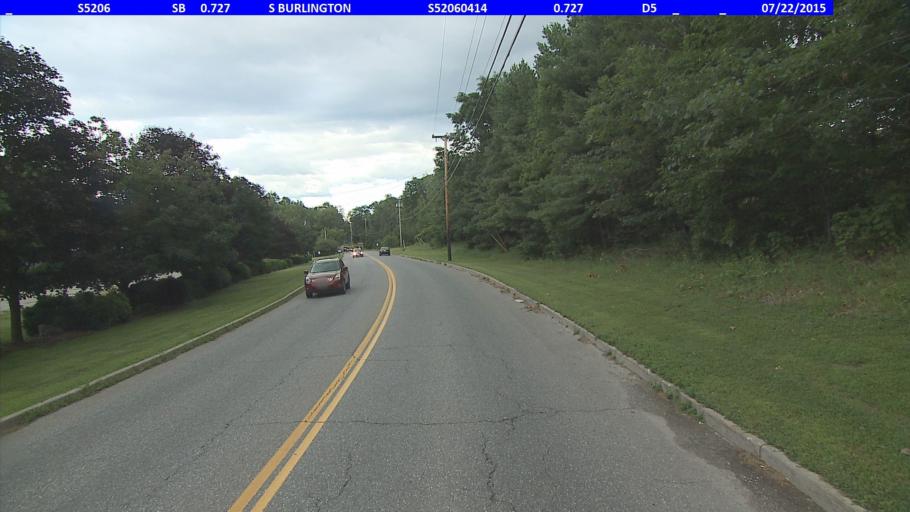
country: US
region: Vermont
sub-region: Chittenden County
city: South Burlington
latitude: 44.4794
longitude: -73.1703
